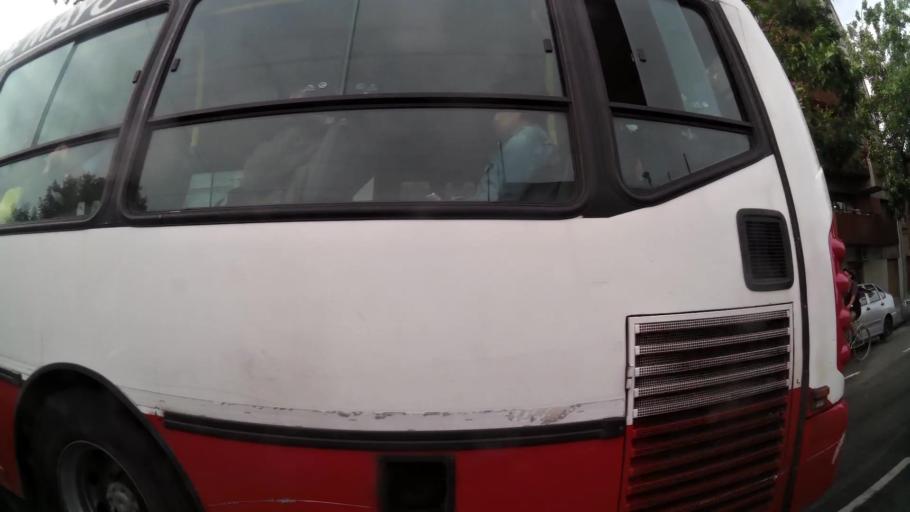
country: AR
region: Buenos Aires F.D.
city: Buenos Aires
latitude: -34.6311
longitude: -58.4236
